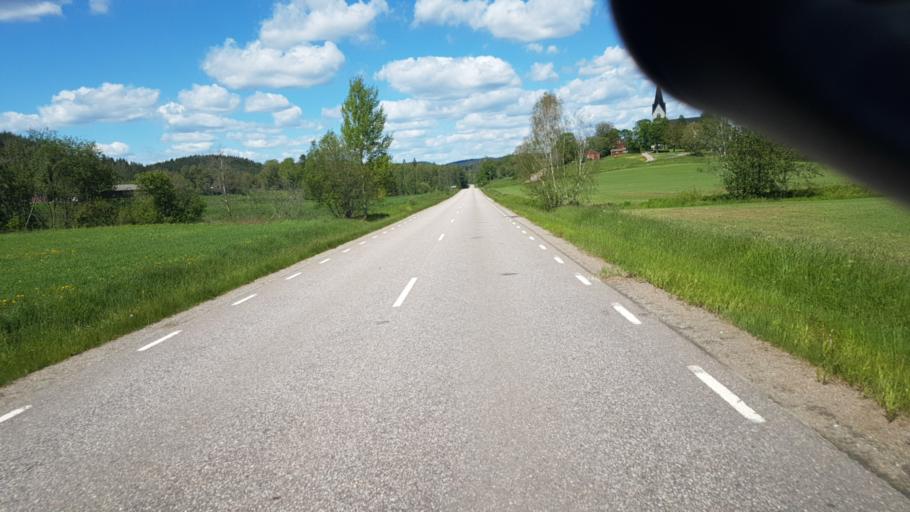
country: SE
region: Vaermland
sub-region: Arvika Kommun
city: Arvika
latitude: 59.6494
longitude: 12.8923
